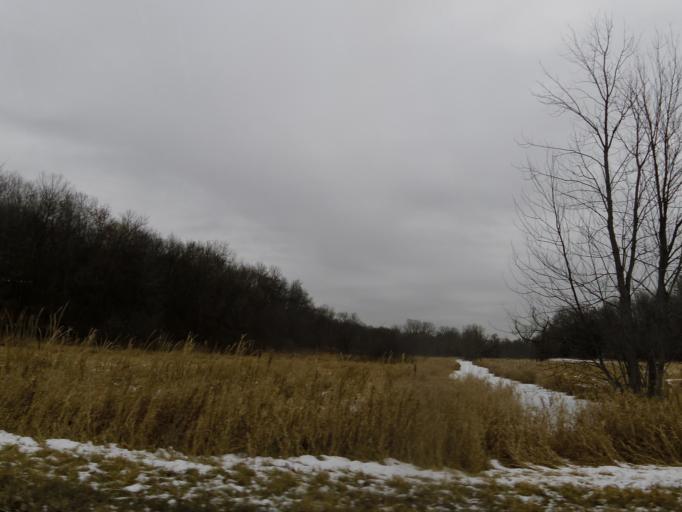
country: US
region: Minnesota
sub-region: Hennepin County
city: Medina
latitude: 45.0144
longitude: -93.5825
